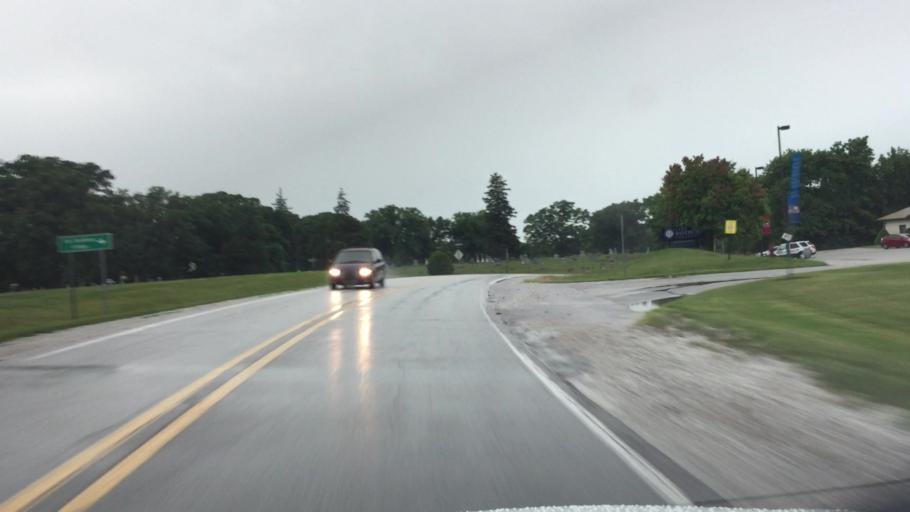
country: US
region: Illinois
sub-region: Hancock County
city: Carthage
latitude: 40.4259
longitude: -91.1392
